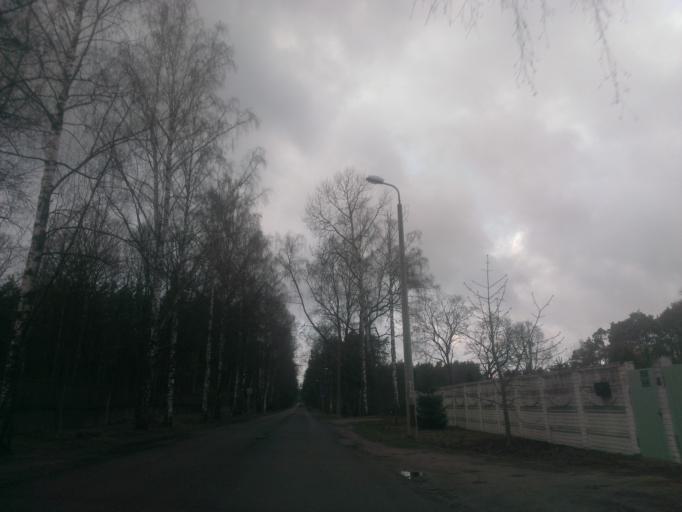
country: LV
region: Riga
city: Bergi
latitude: 56.9916
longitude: 24.2893
